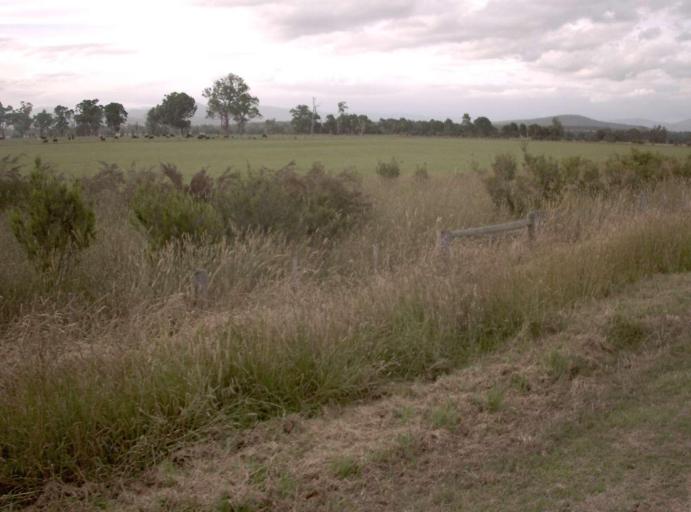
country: AU
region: Victoria
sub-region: Wellington
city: Sale
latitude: -37.8456
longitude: 147.0550
